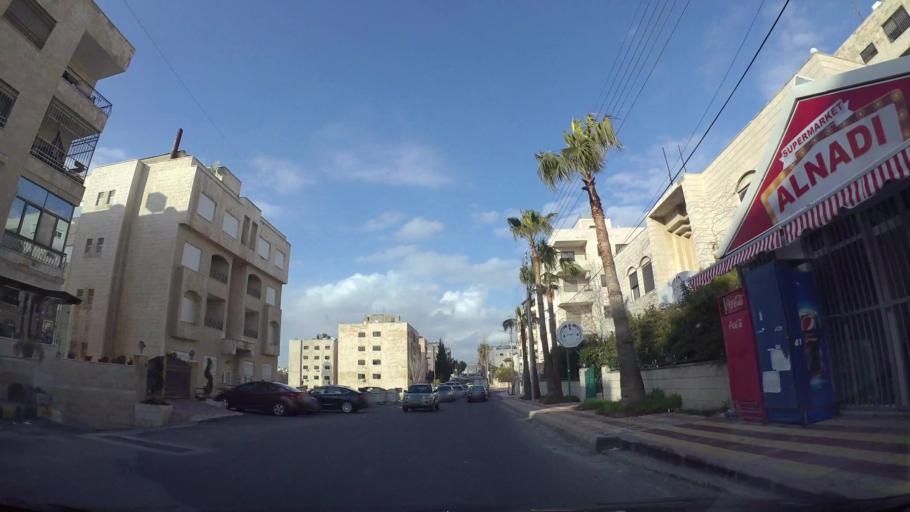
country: JO
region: Amman
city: Al Jubayhah
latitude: 31.9844
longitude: 35.8695
